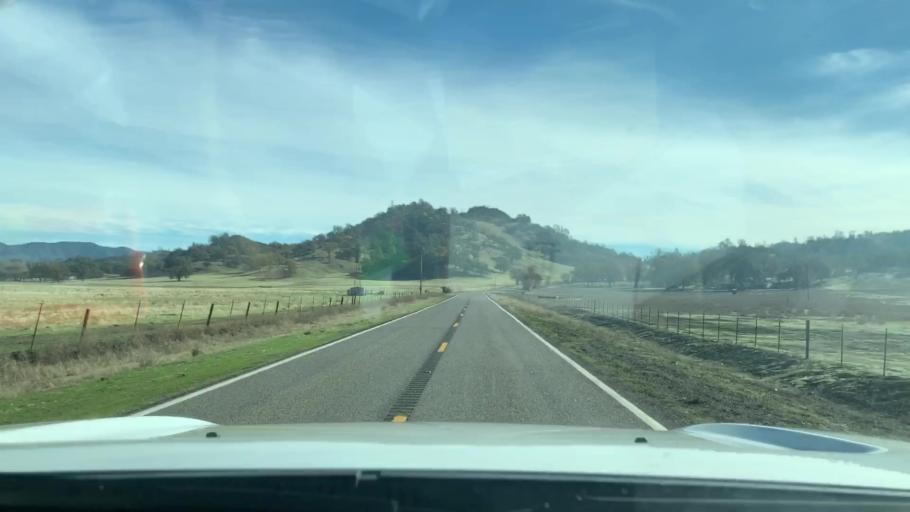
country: US
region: California
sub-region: Fresno County
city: Coalinga
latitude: 36.1745
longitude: -120.6778
